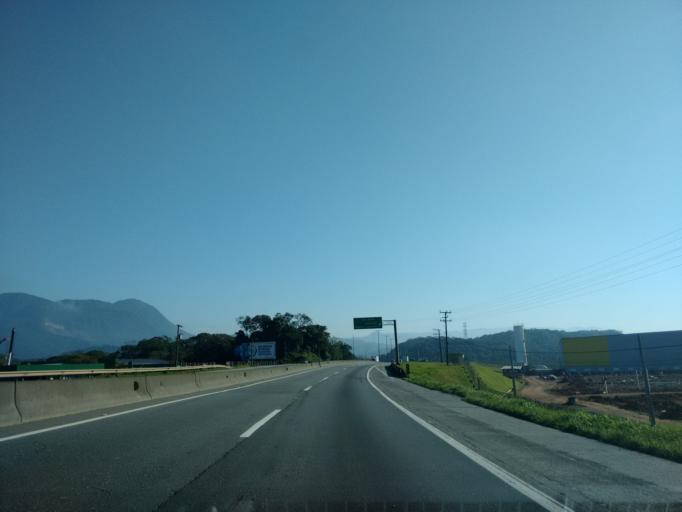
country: BR
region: Santa Catarina
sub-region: Joinville
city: Joinville
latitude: -26.2606
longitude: -48.9033
